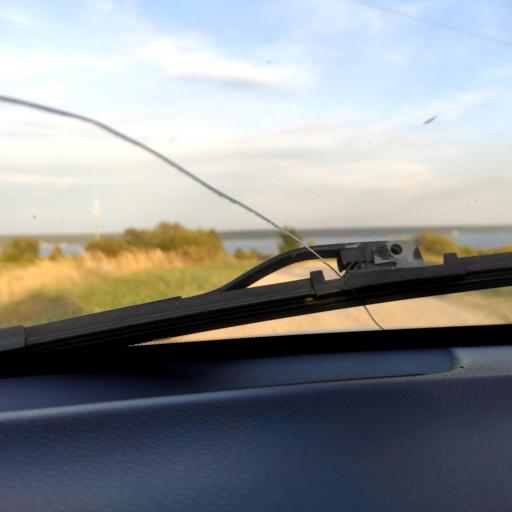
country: RU
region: Tatarstan
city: Verkhniy Uslon
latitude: 55.6483
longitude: 48.9391
